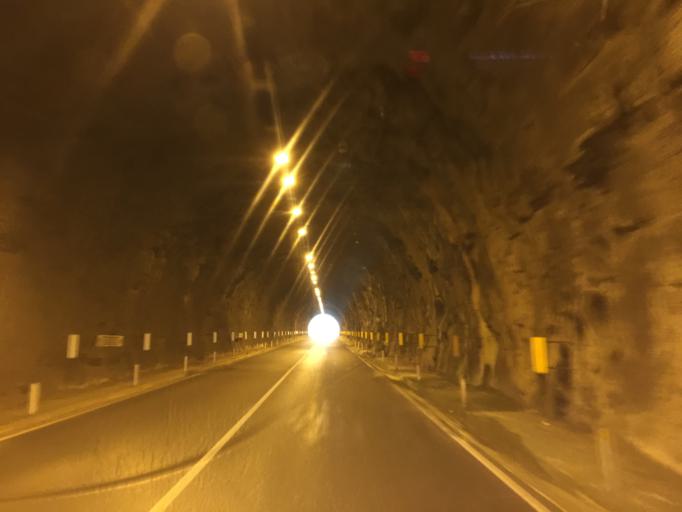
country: ES
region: Asturias
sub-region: Province of Asturias
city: Proaza
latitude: 43.2320
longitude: -6.0339
